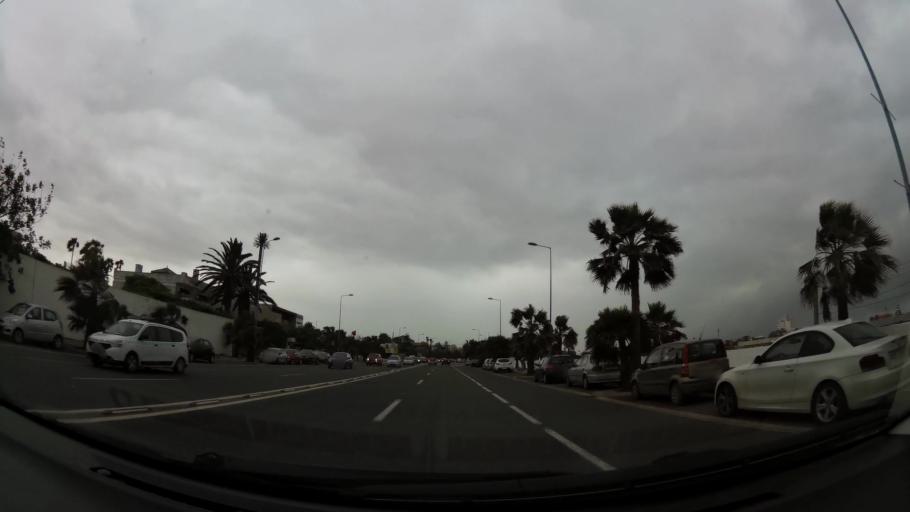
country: MA
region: Grand Casablanca
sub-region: Casablanca
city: Casablanca
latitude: 33.5947
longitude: -7.6704
